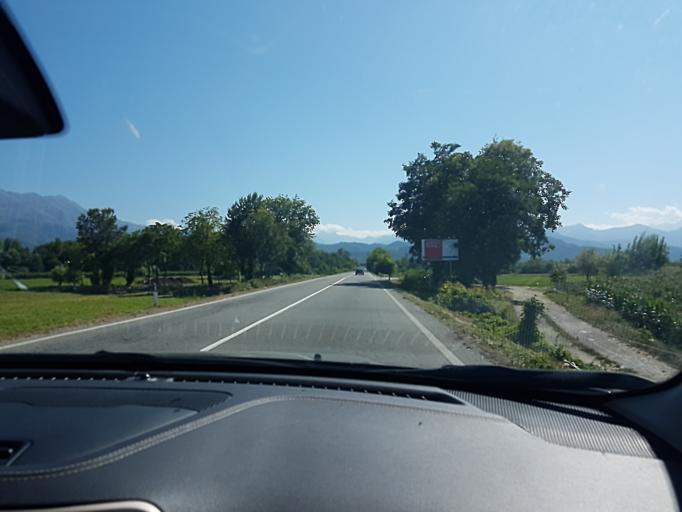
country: IT
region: Piedmont
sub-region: Provincia di Cuneo
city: Cuneo
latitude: 44.3635
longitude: 7.5506
